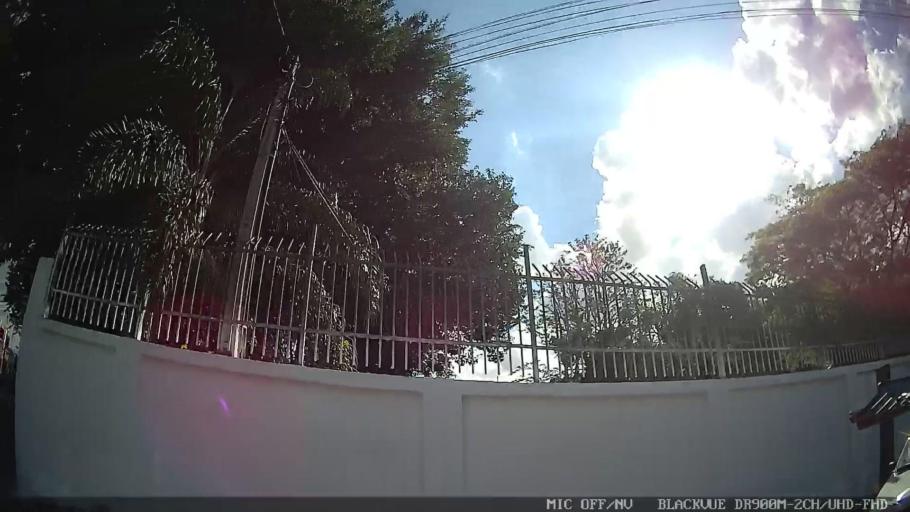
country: BR
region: Sao Paulo
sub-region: Ferraz De Vasconcelos
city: Ferraz de Vasconcelos
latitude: -23.5344
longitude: -46.3940
